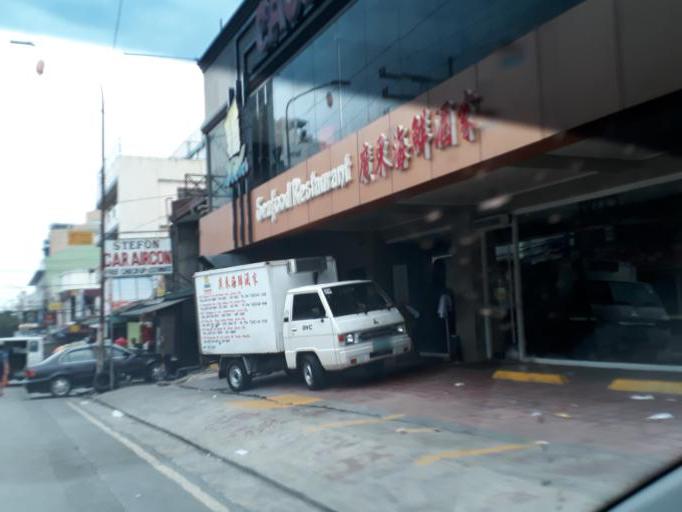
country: PH
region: Calabarzon
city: Del Monte
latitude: 14.6382
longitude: 121.0009
